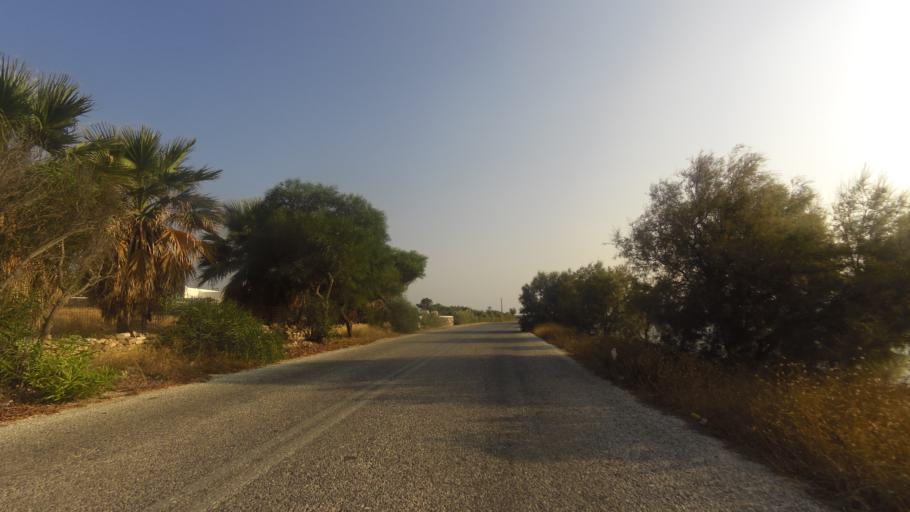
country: GR
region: South Aegean
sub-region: Nomos Kykladon
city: Antiparos
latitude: 37.0114
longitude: 25.0751
